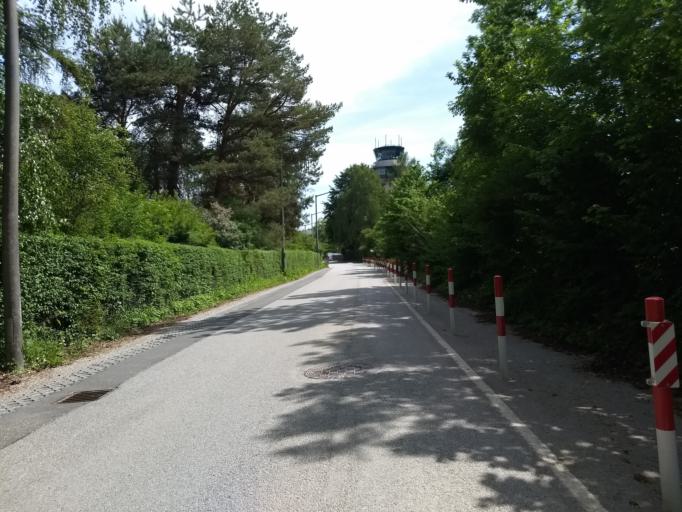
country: DE
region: Bavaria
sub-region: Upper Bavaria
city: Freilassing
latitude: 47.7953
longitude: 12.9947
